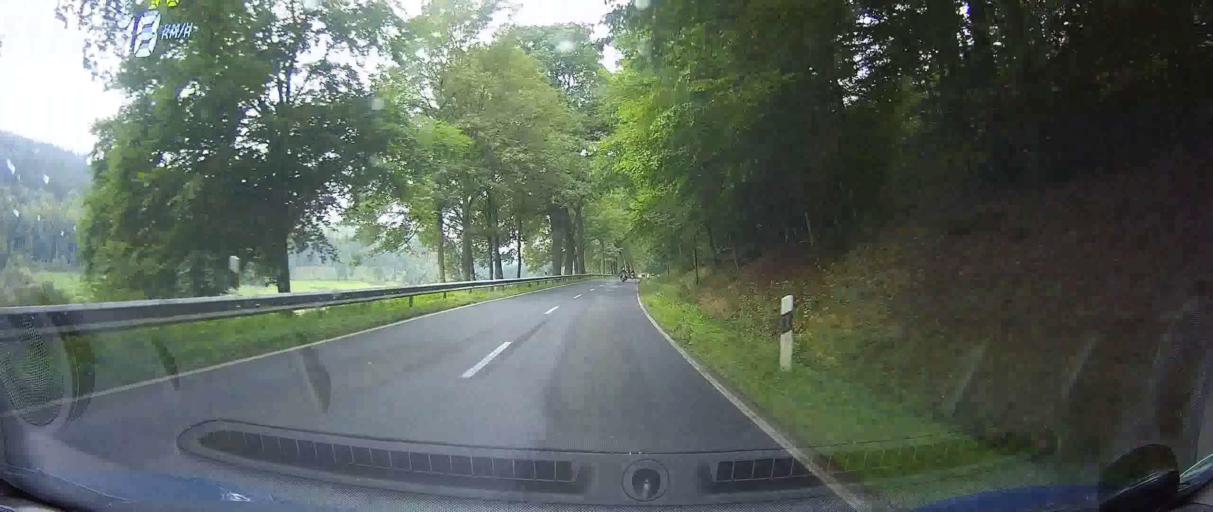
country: DE
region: Lower Saxony
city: Uslar
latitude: 51.6945
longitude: 9.6283
